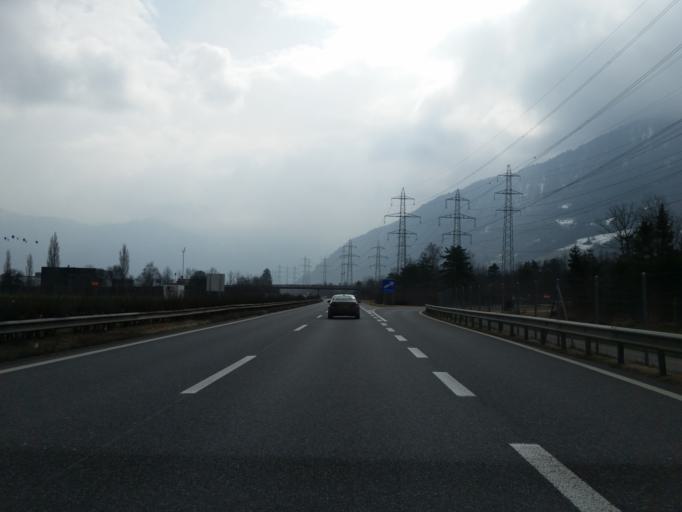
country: CH
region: Grisons
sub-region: Landquart District
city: Maienfeld
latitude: 47.0044
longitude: 9.5188
